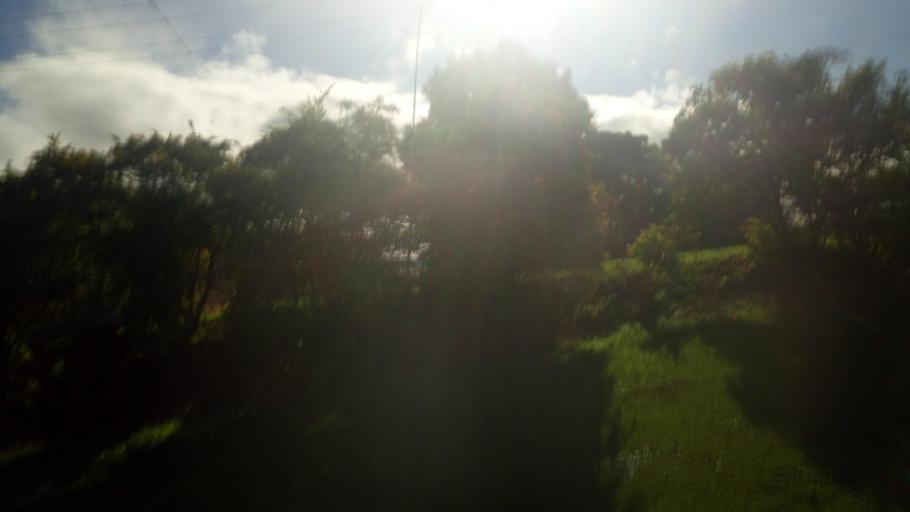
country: AU
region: Queensland
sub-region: Cassowary Coast
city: Innisfail
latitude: -17.5185
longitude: 145.9877
